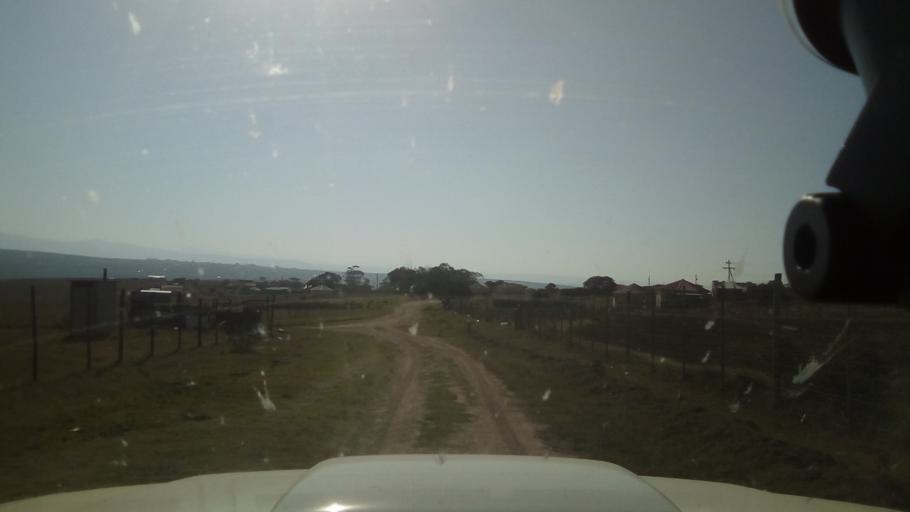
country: ZA
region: Eastern Cape
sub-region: Buffalo City Metropolitan Municipality
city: Bhisho
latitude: -32.9386
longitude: 27.3356
